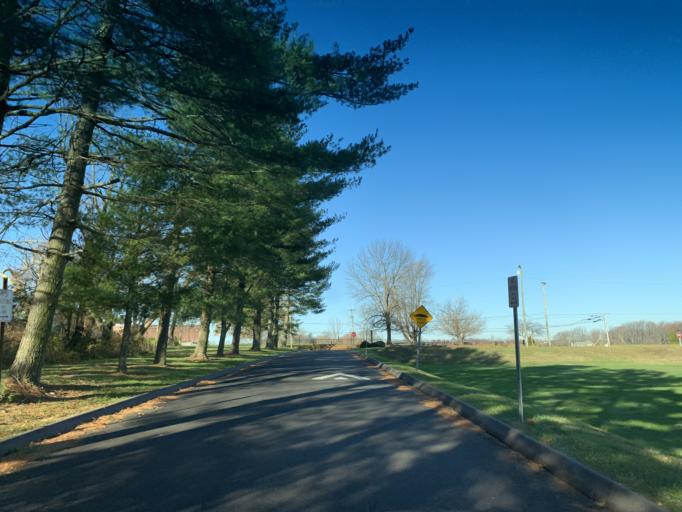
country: US
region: Maryland
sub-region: Harford County
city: Riverside
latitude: 39.5614
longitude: -76.2426
